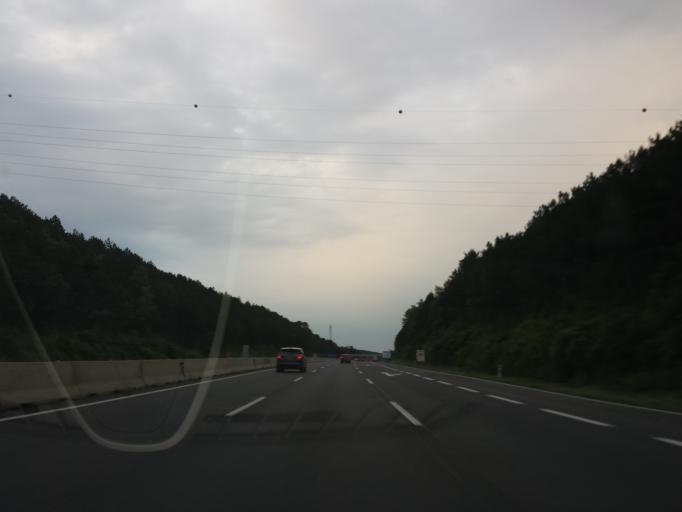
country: AT
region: Lower Austria
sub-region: Politischer Bezirk Wiener Neustadt
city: Theresienfeld
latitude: 47.8498
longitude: 16.1821
